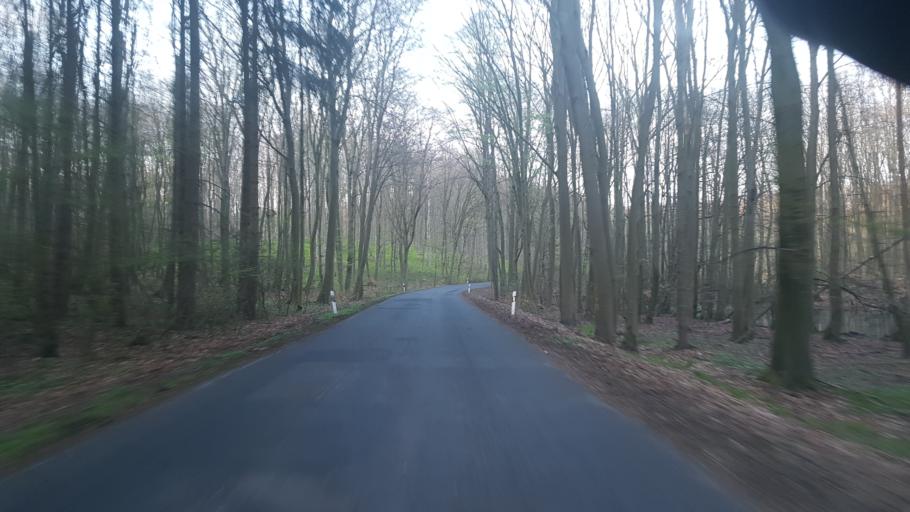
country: DE
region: Brandenburg
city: Gramzow
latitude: 53.1808
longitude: 13.9068
